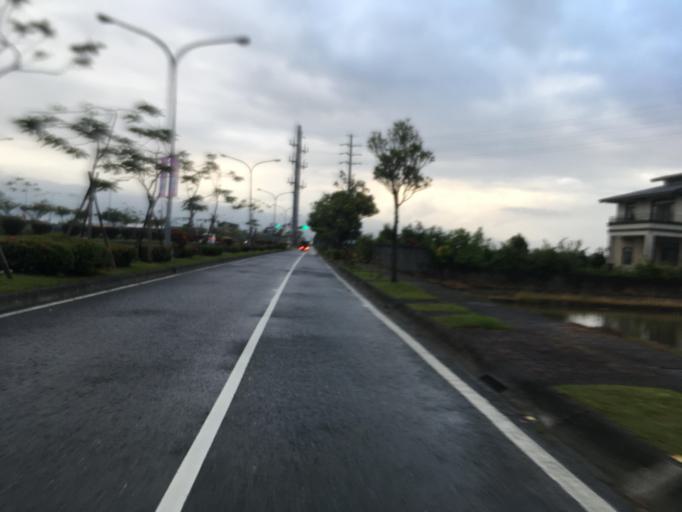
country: TW
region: Taiwan
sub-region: Yilan
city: Yilan
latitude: 24.7293
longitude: 121.7721
